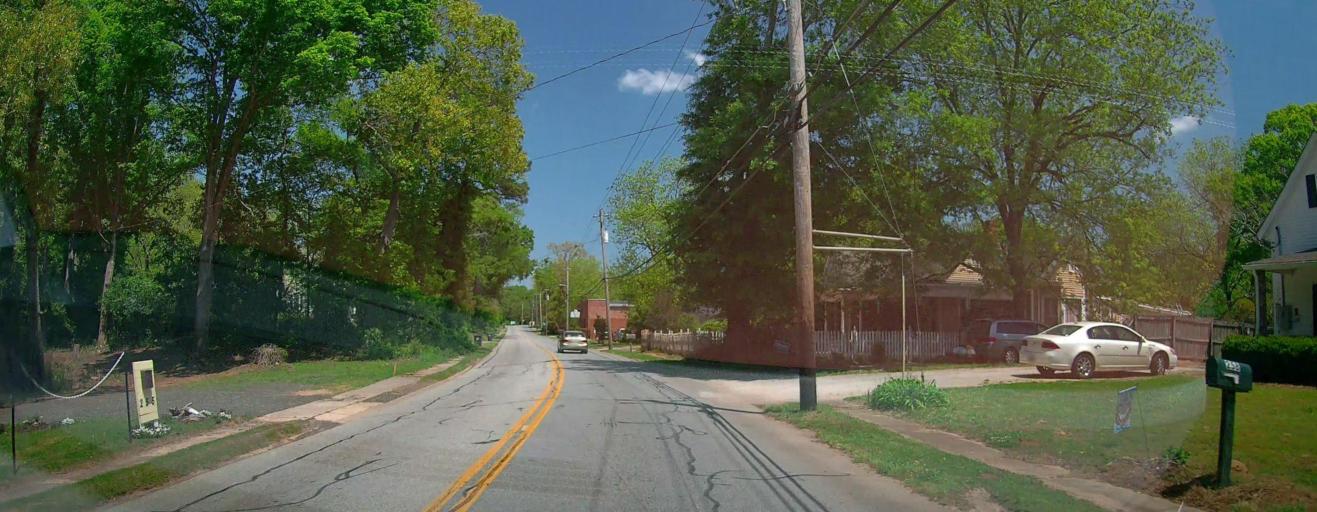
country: US
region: Georgia
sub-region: Jasper County
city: Monticello
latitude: 33.3078
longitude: -83.6804
